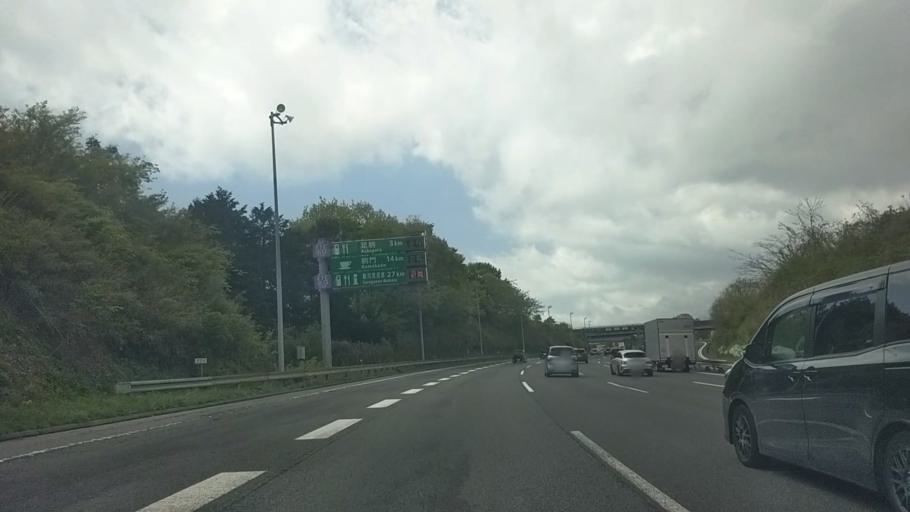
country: JP
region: Shizuoka
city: Gotemba
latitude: 35.3403
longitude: 138.9777
